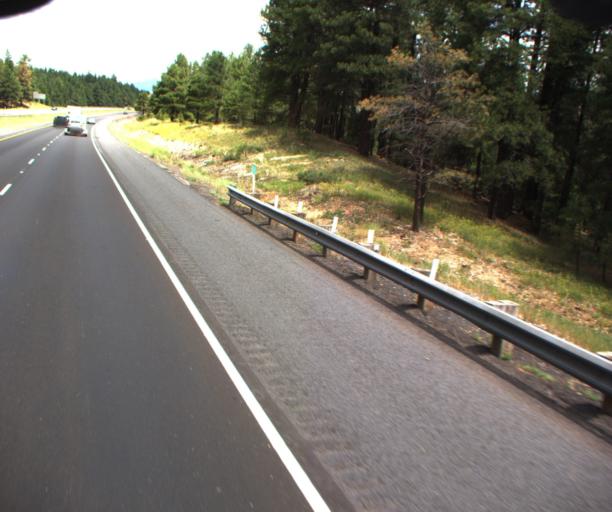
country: US
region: Arizona
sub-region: Coconino County
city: Kachina Village
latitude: 35.1091
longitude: -111.6812
